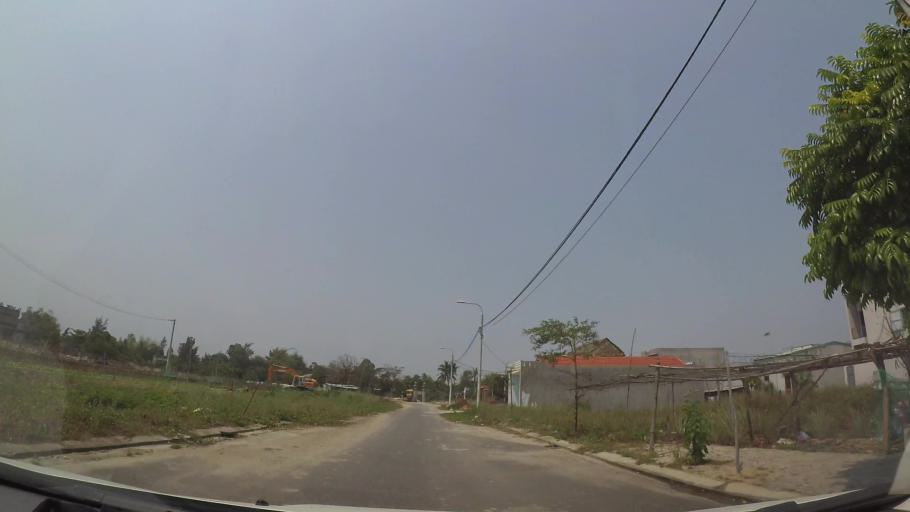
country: VN
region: Da Nang
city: Ngu Hanh Son
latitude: 15.9849
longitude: 108.2596
